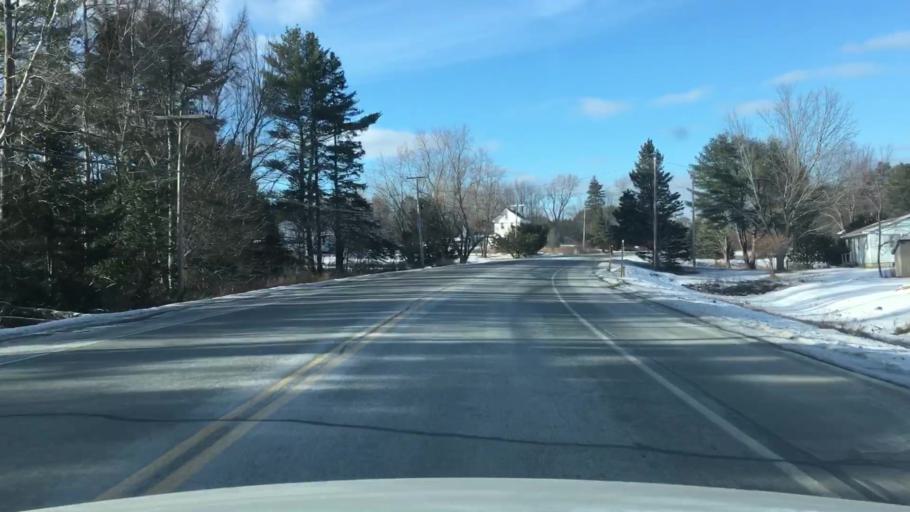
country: US
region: Maine
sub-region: Penobscot County
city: Eddington
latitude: 44.8184
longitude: -68.6466
